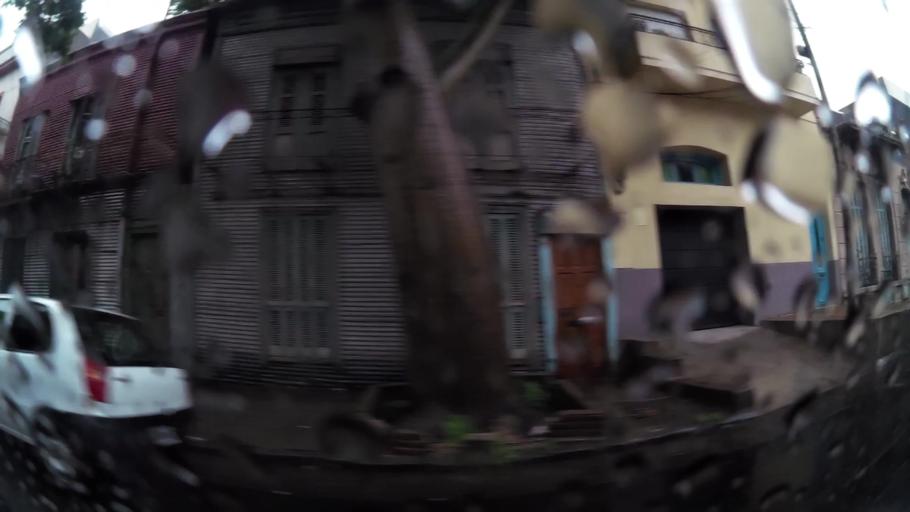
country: AR
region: Buenos Aires
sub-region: Partido de Avellaneda
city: Avellaneda
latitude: -34.6433
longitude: -58.3643
